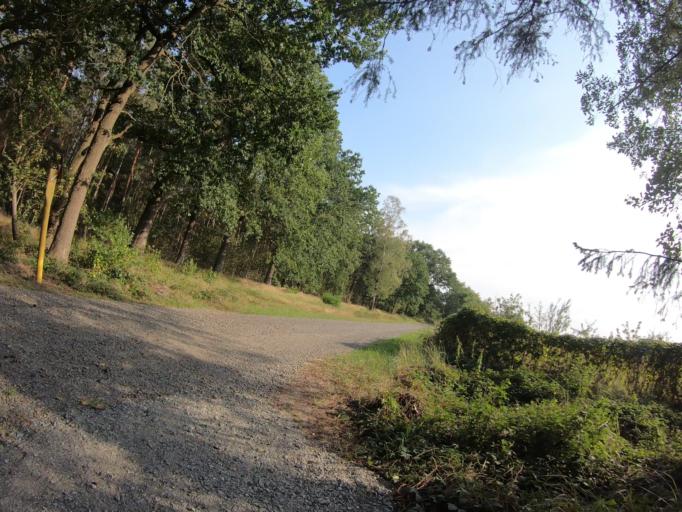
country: DE
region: Lower Saxony
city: Gifhorn
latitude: 52.4581
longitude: 10.5583
